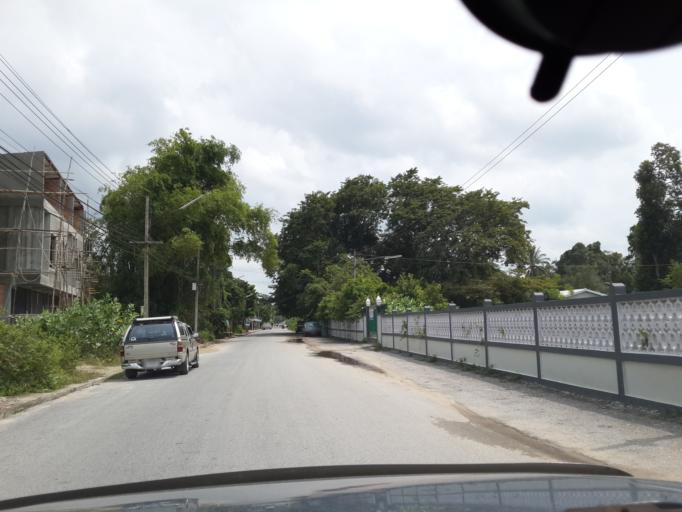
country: TH
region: Pattani
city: Pattani
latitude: 6.8555
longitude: 101.2543
